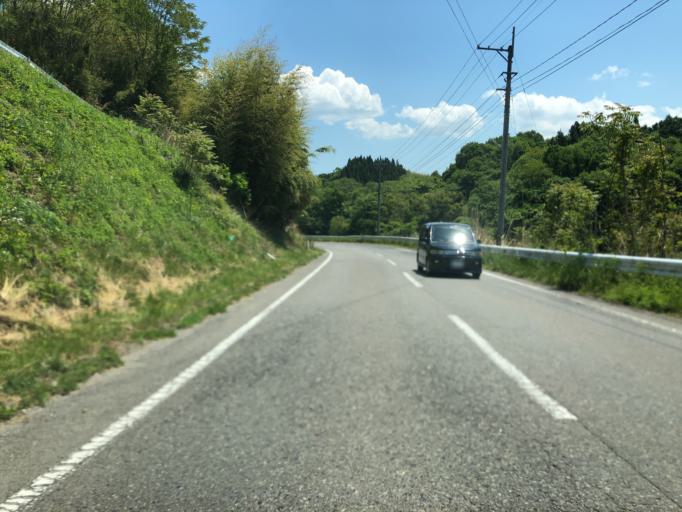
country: JP
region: Fukushima
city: Funehikimachi-funehiki
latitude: 37.4800
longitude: 140.5684
